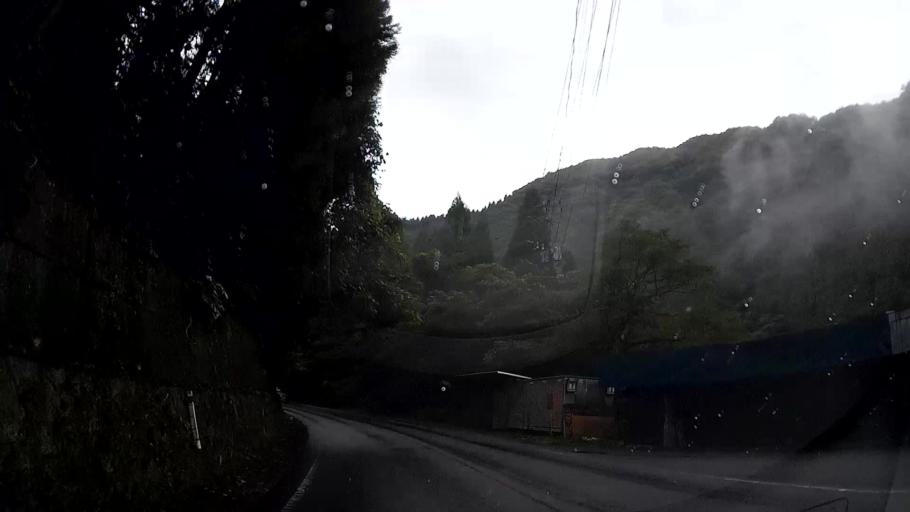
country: JP
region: Oita
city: Hita
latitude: 33.1781
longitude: 131.0152
